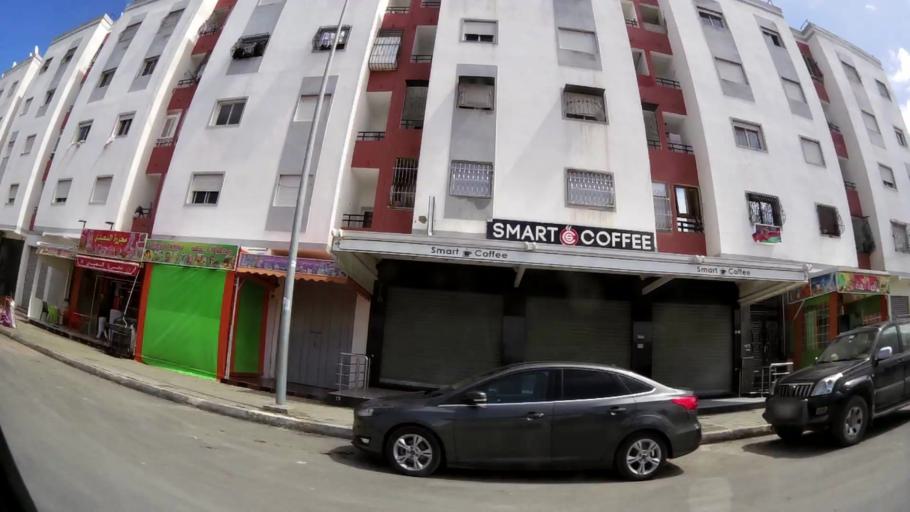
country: MA
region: Grand Casablanca
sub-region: Mediouna
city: Tit Mellil
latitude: 33.6066
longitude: -7.4806
